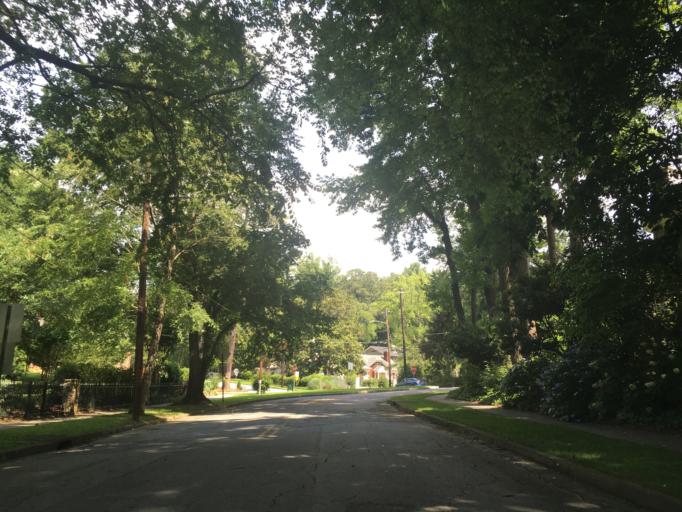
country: US
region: Georgia
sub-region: DeKalb County
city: Druid Hills
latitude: 33.7966
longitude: -84.3597
